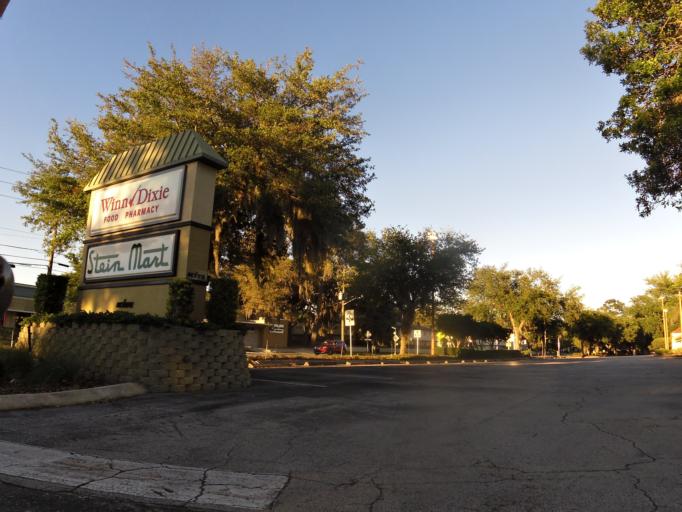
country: US
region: Florida
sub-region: Duval County
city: Jacksonville
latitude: 30.2630
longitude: -81.6448
